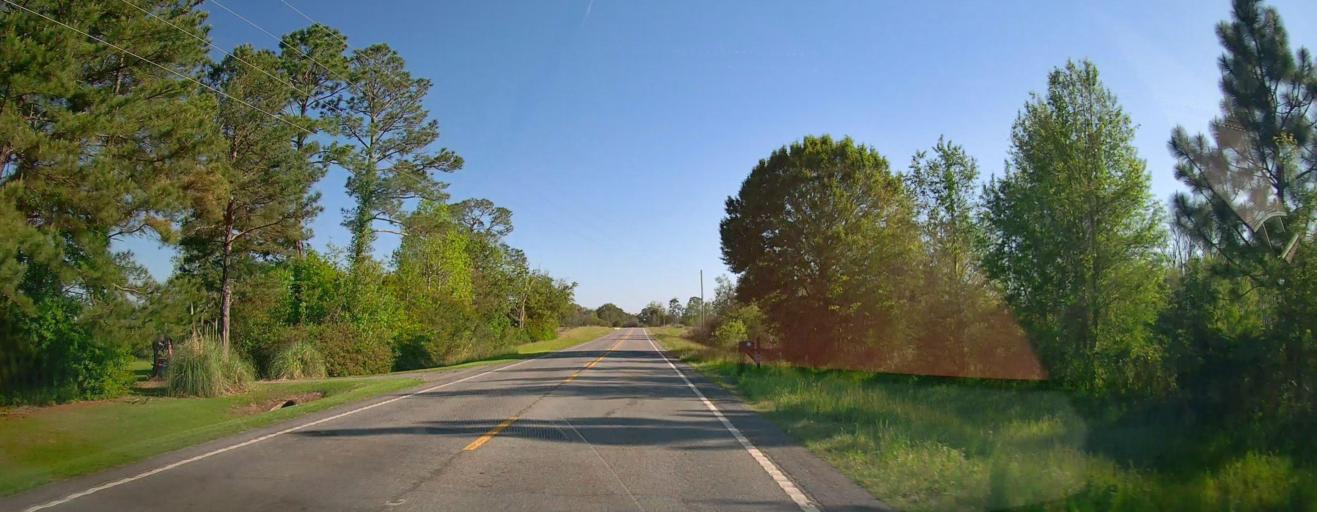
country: US
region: Georgia
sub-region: Ben Hill County
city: Fitzgerald
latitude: 31.7150
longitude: -83.3100
